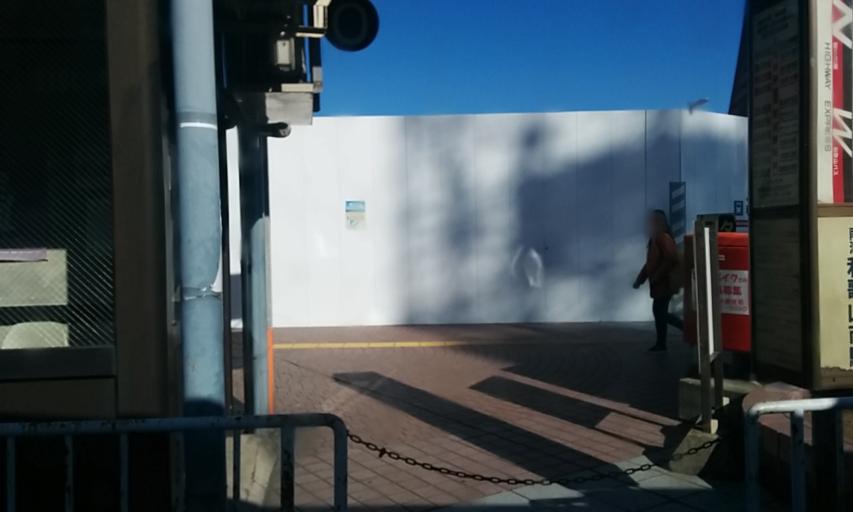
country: JP
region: Wakayama
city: Wakayama-shi
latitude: 34.2360
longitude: 135.1669
